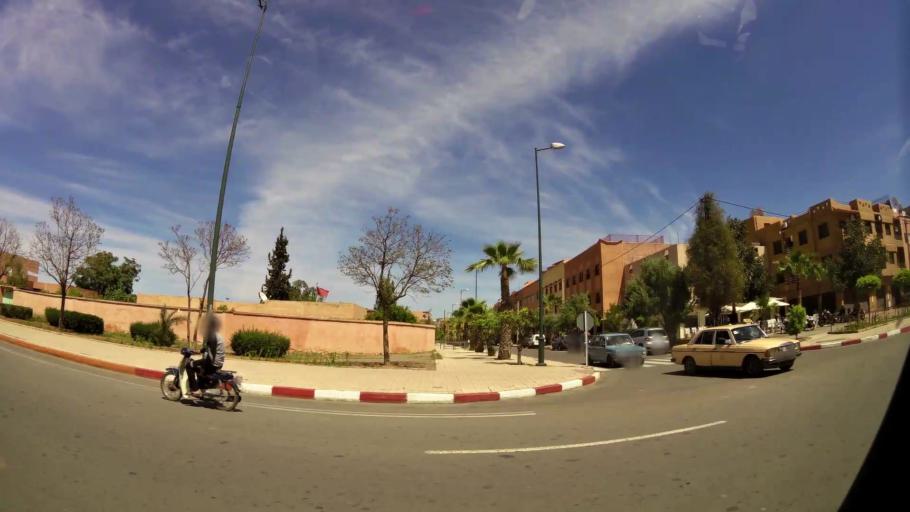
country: MA
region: Marrakech-Tensift-Al Haouz
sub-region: Marrakech
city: Marrakesh
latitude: 31.6082
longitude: -7.9729
